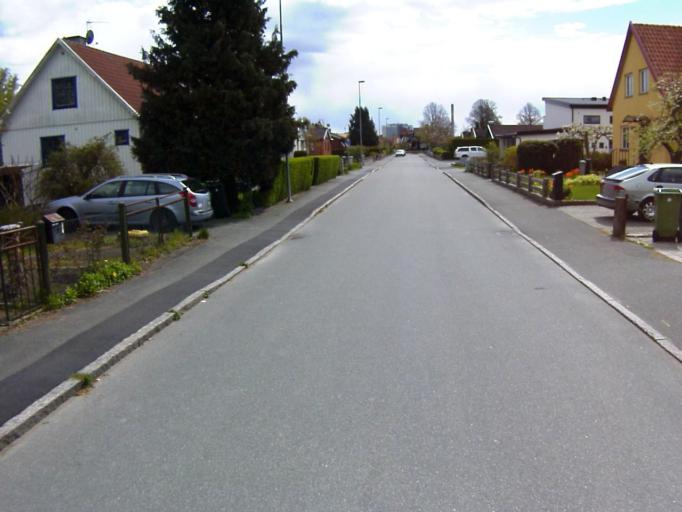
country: SE
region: Skane
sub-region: Kristianstads Kommun
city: Kristianstad
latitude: 56.0417
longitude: 14.1708
